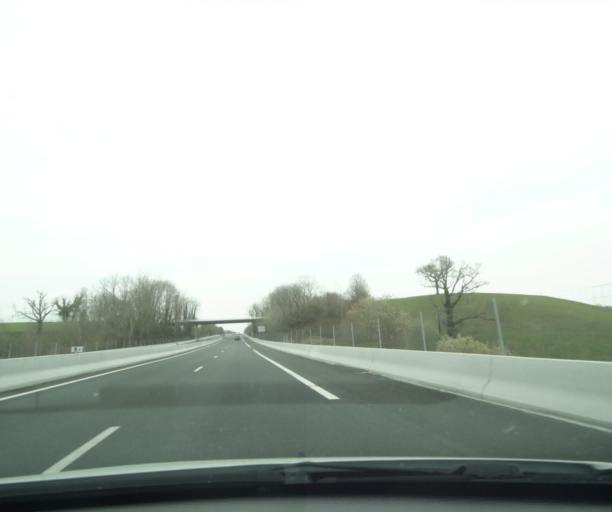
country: FR
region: Aquitaine
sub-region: Departement des Pyrenees-Atlantiques
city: Briscous
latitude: 43.4496
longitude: -1.3513
